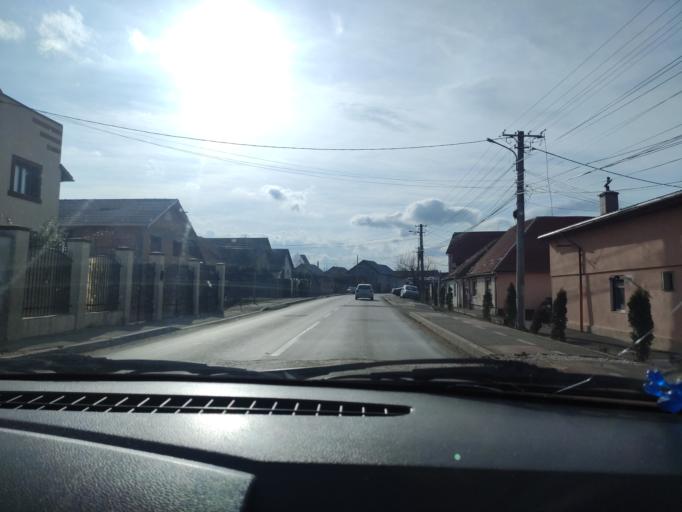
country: RO
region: Brasov
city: Codlea
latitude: 45.7029
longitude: 25.4564
